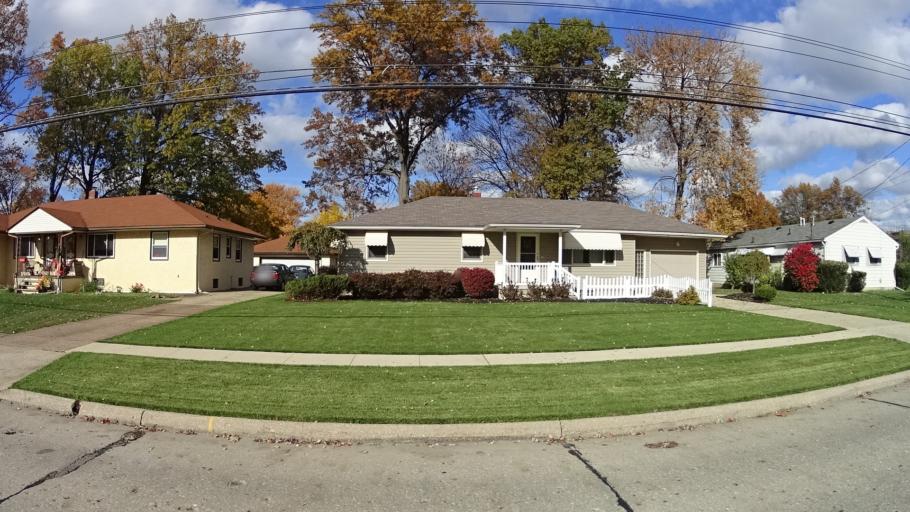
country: US
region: Ohio
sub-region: Lorain County
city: Lorain
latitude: 41.4361
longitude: -82.1904
